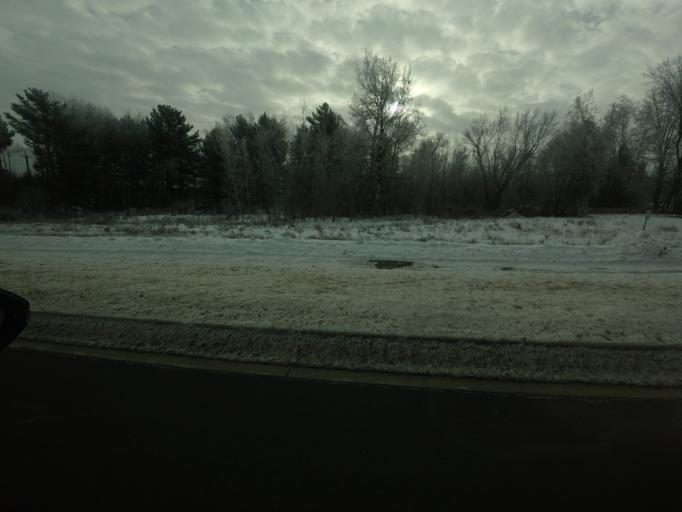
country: CA
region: New Brunswick
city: Oromocto
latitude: 45.8485
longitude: -66.4963
